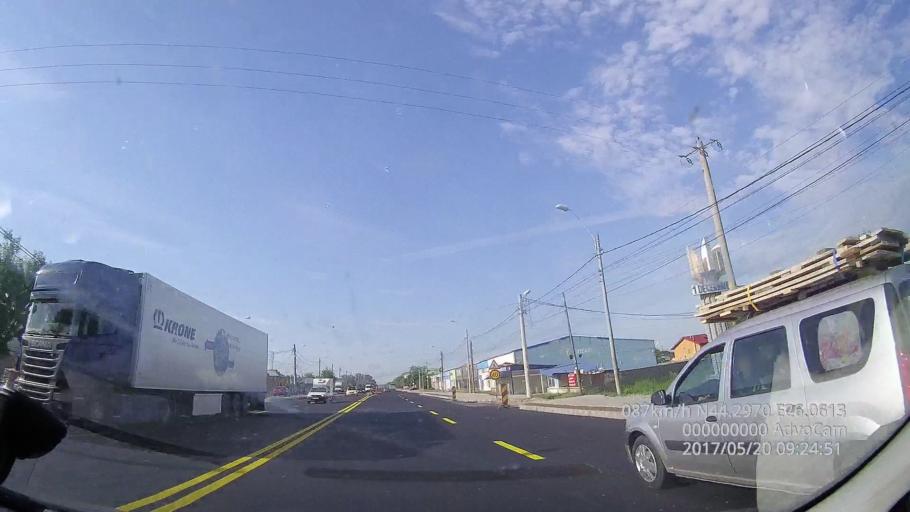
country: RO
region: Ilfov
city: Prim Decembrie
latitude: 44.2969
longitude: 26.0614
